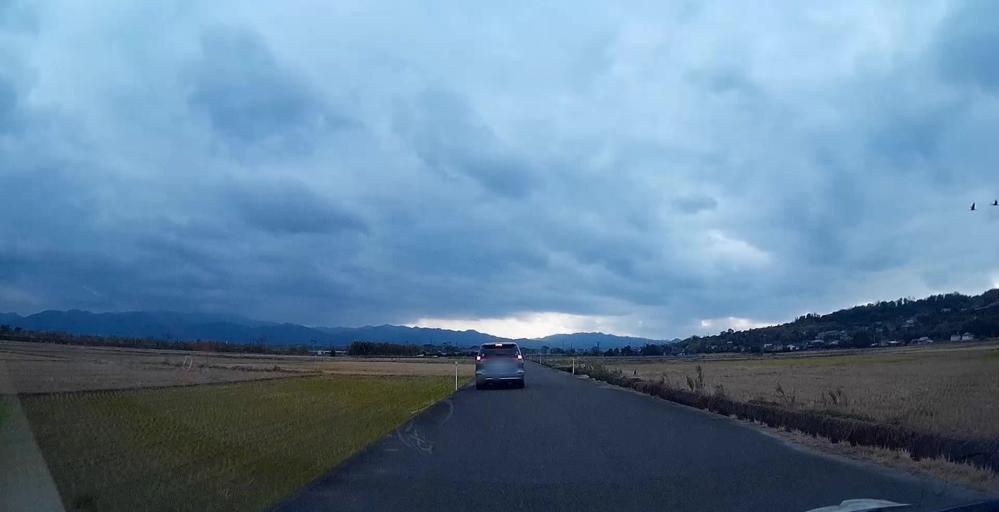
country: JP
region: Kagoshima
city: Izumi
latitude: 32.0996
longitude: 130.2753
